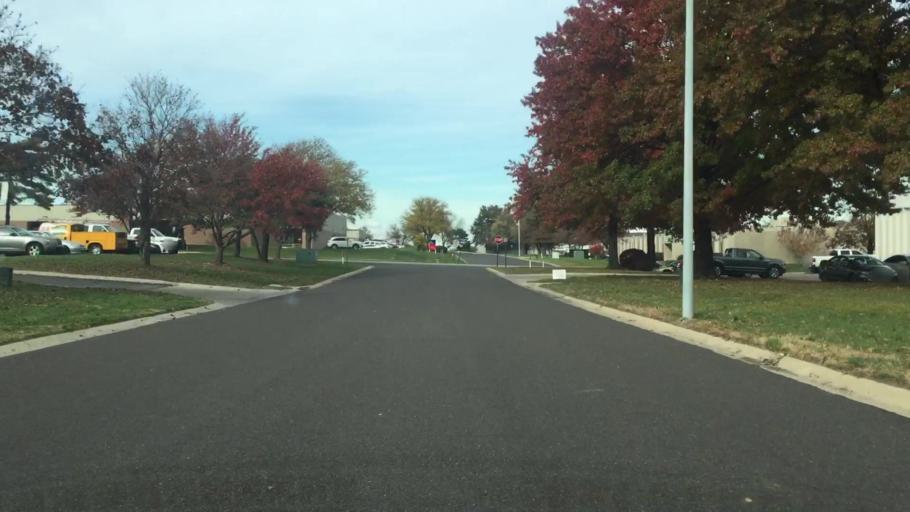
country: US
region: Kansas
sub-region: Johnson County
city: Lenexa
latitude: 38.9629
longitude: -94.7213
